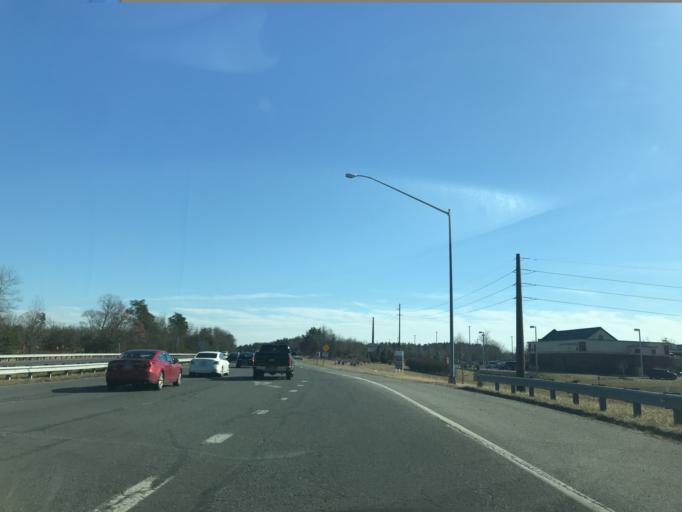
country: US
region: Maryland
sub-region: Prince George's County
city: Accokeek
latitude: 38.6631
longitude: -77.0171
